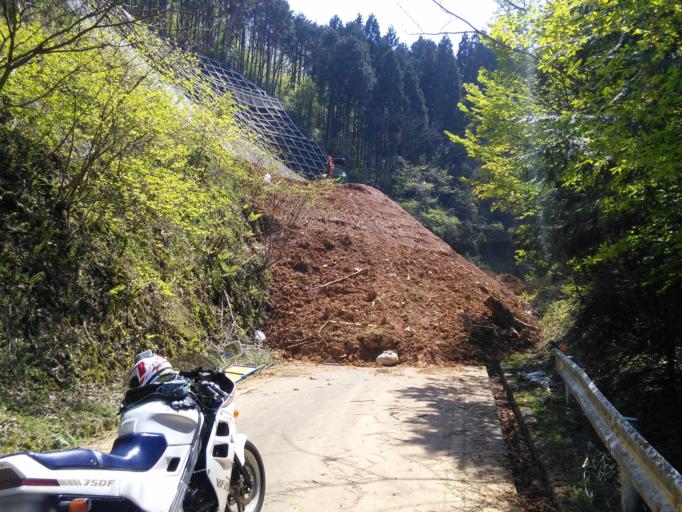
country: JP
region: Kyoto
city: Ayabe
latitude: 35.2558
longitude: 135.3264
